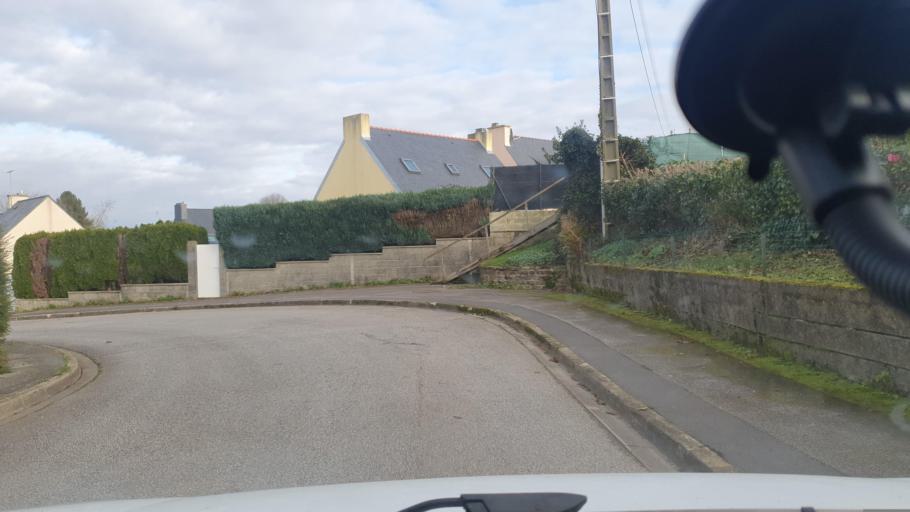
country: FR
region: Brittany
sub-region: Departement du Finistere
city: Briec
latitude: 48.1032
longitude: -4.0078
